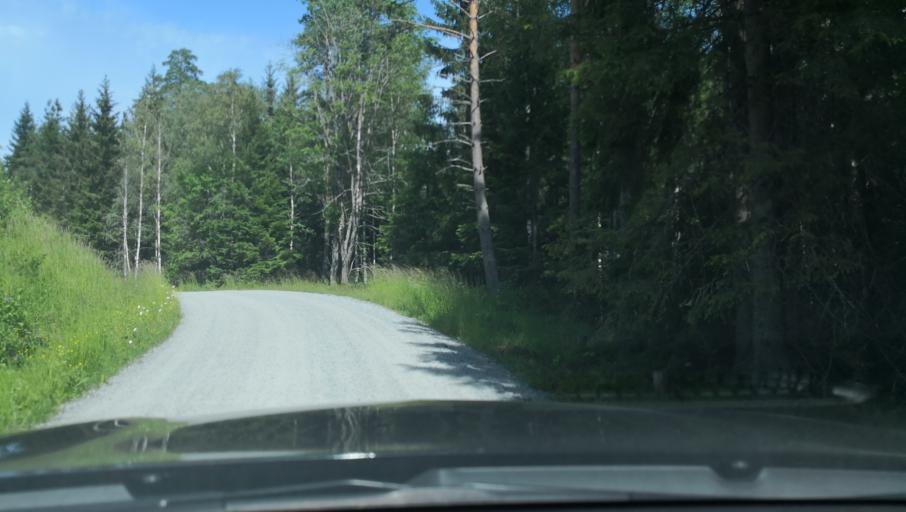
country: SE
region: Vaestmanland
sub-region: Surahammars Kommun
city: Ramnas
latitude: 59.8907
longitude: 16.0999
